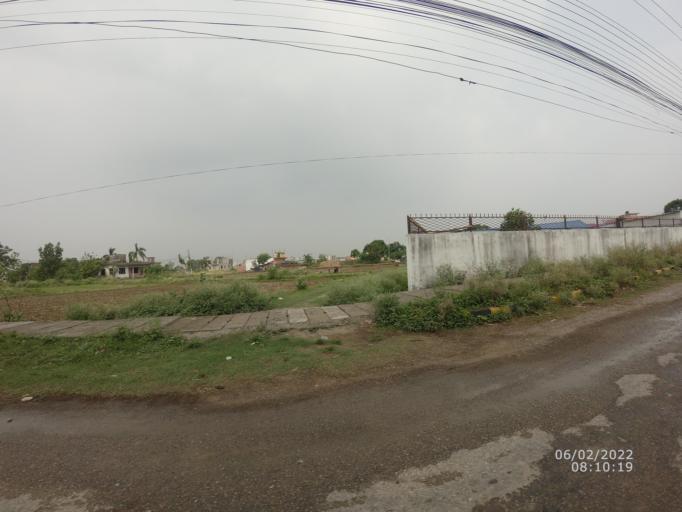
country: NP
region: Western Region
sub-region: Lumbini Zone
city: Bhairahawa
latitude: 27.4920
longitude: 83.4603
